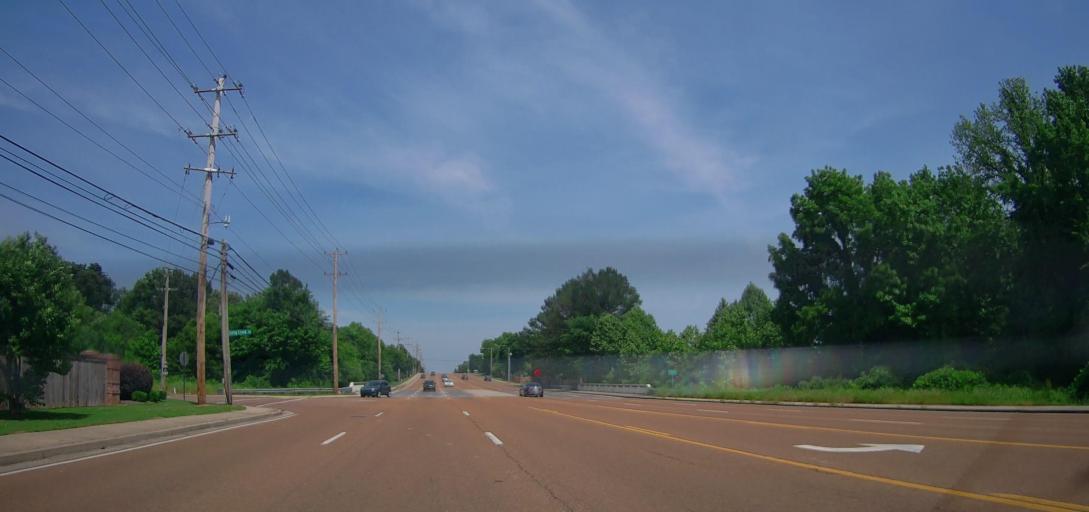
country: US
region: Mississippi
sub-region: De Soto County
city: Olive Branch
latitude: 35.0205
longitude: -89.8093
